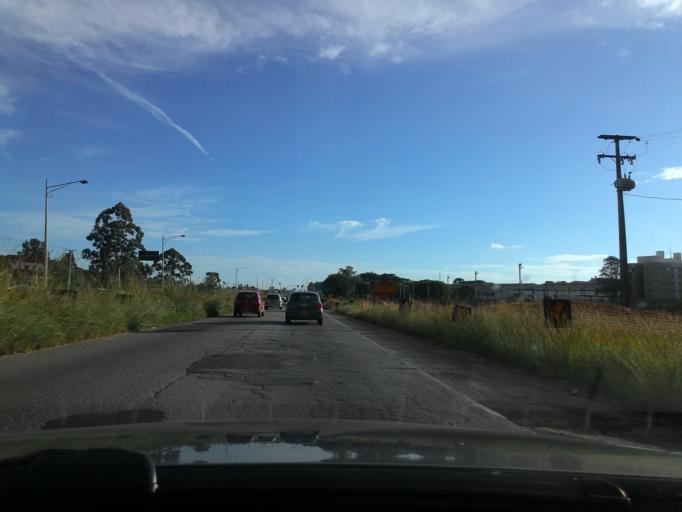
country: BR
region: Parana
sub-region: Pinhais
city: Pinhais
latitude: -25.4060
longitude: -49.2186
